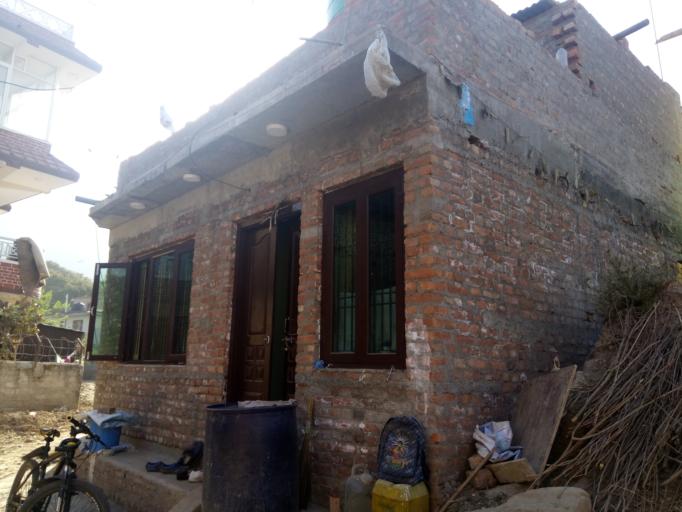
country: NP
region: Central Region
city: Kirtipur
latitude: 27.6693
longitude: 85.2632
